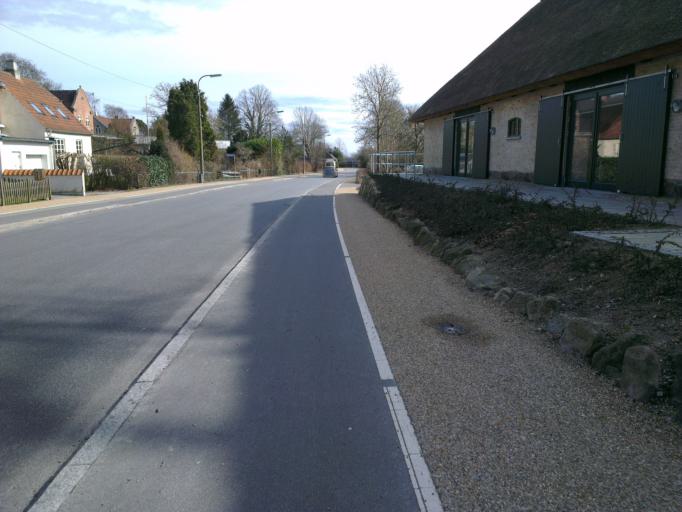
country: DK
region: Capital Region
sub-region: Frederikssund Kommune
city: Skibby
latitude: 55.7487
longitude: 11.9602
